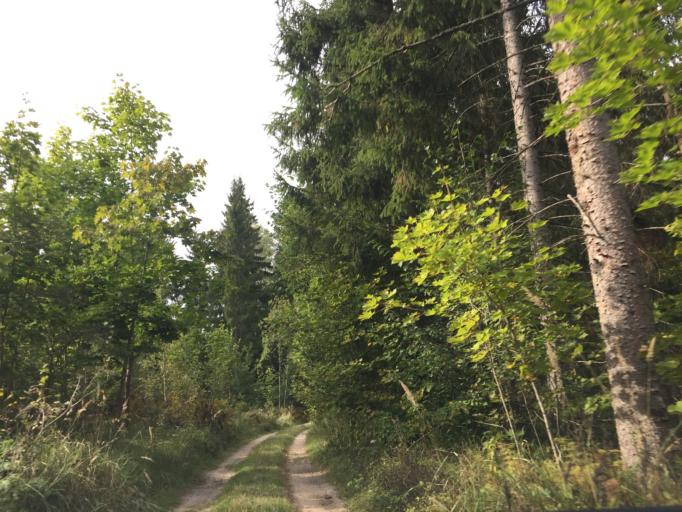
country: LV
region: Ikskile
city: Ikskile
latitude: 56.7618
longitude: 24.4704
